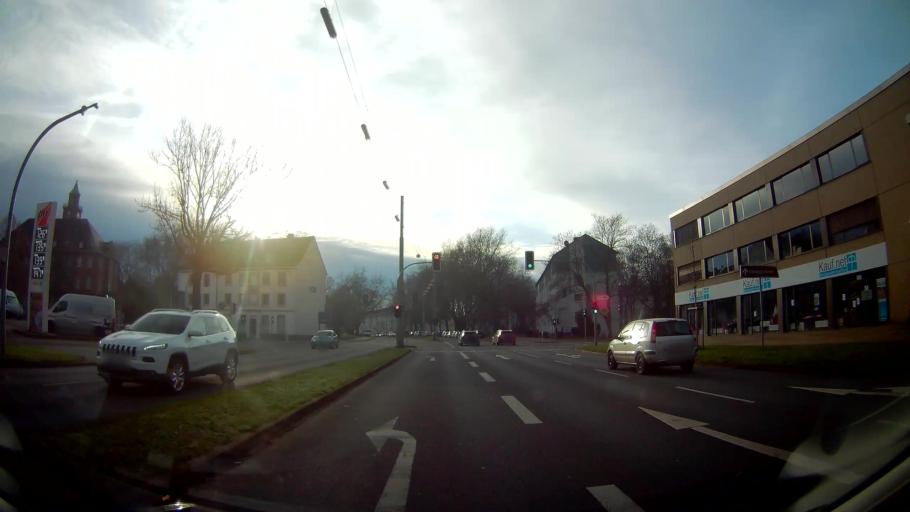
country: DE
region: North Rhine-Westphalia
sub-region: Regierungsbezirk Arnsberg
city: Herne
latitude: 51.5391
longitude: 7.2179
